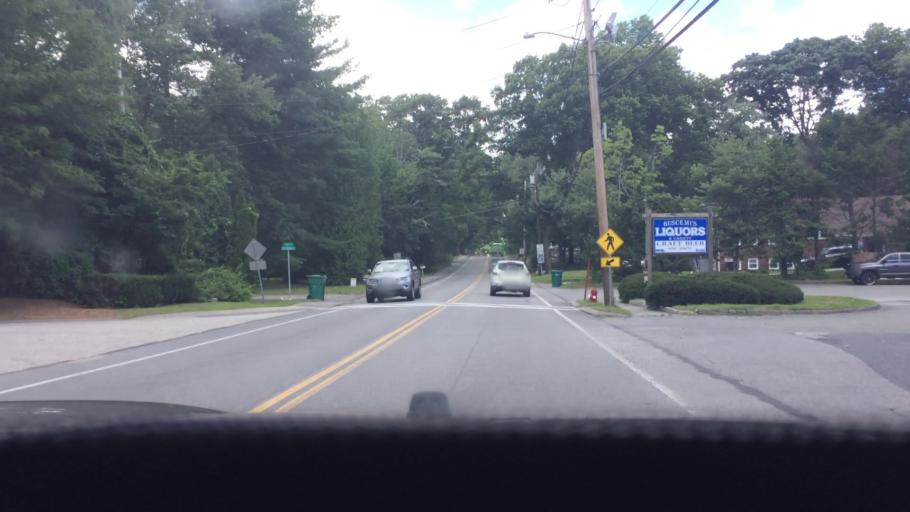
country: US
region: Massachusetts
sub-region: Middlesex County
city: Maynard
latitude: 42.4508
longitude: -71.4543
